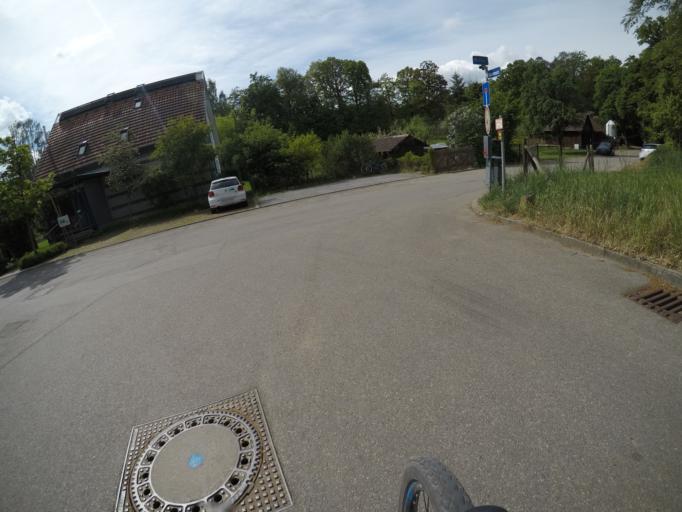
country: DE
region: Baden-Wuerttemberg
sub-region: Tuebingen Region
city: Tuebingen
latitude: 48.5403
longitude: 9.0067
